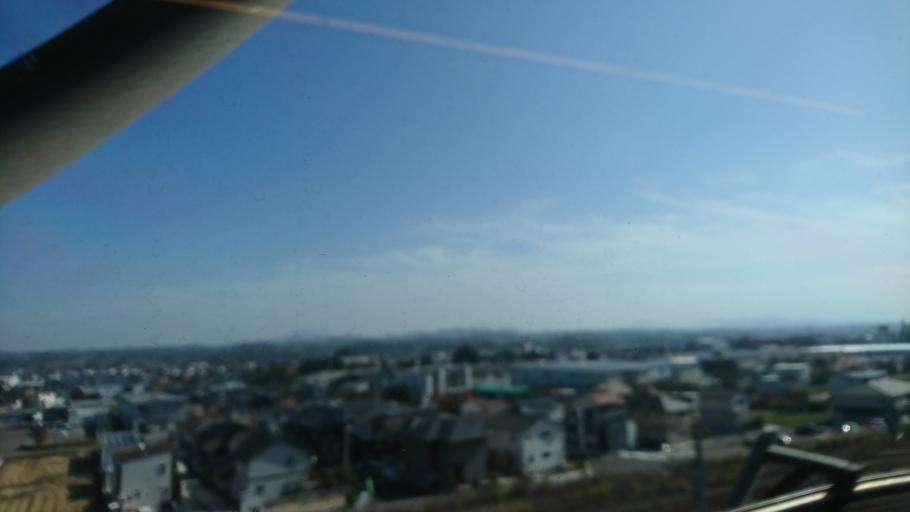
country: JP
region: Fukushima
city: Koriyama
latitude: 37.4225
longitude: 140.3962
